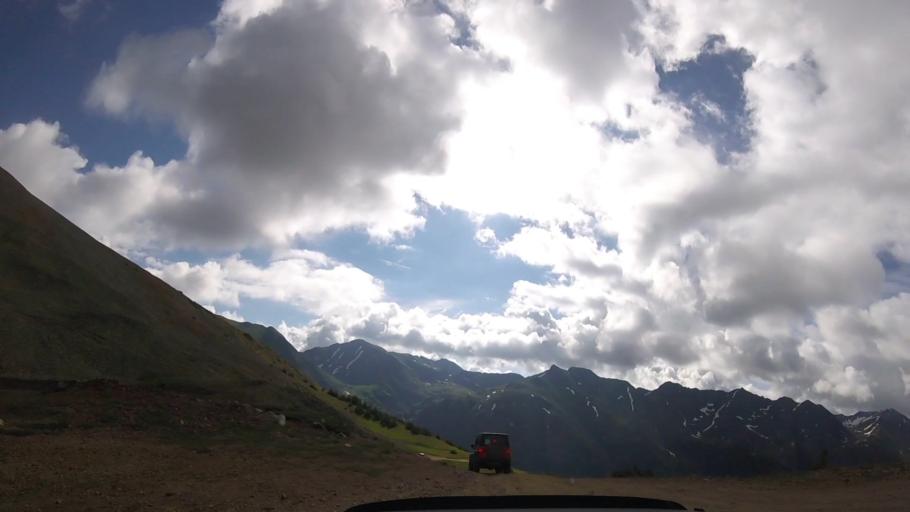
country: US
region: Colorado
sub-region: San Juan County
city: Silverton
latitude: 37.9066
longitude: -107.6606
